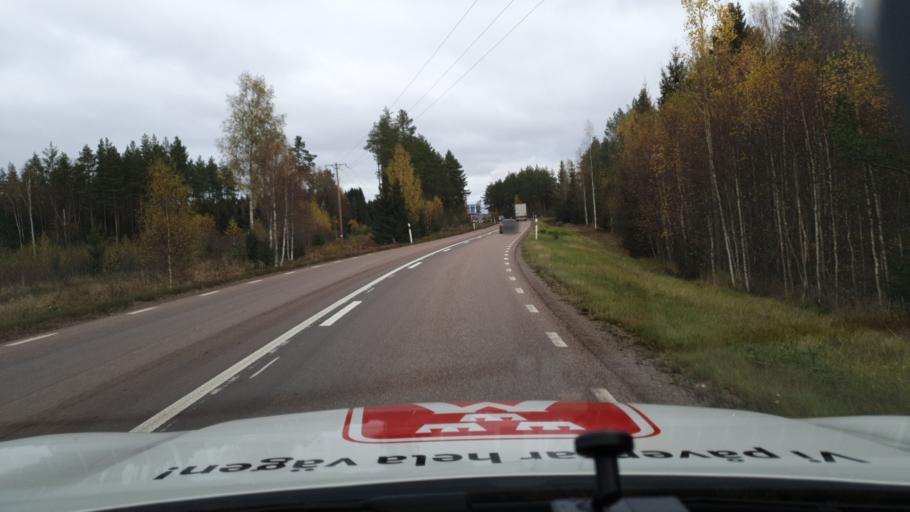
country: SE
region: Gaevleborg
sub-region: Gavle Kommun
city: Hedesunda
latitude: 60.5304
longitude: 16.9423
